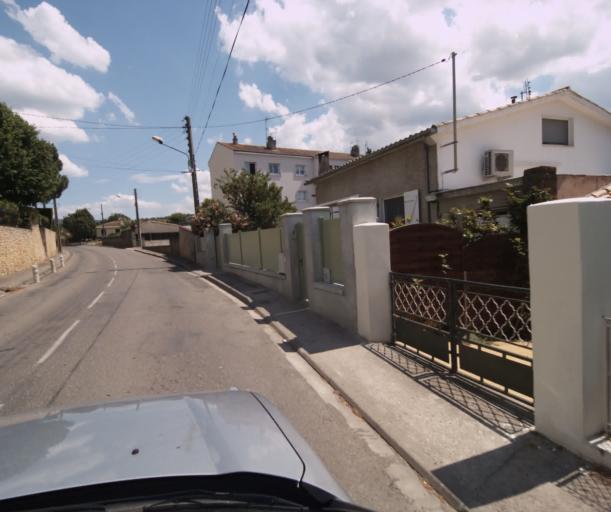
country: FR
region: Languedoc-Roussillon
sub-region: Departement de l'Aude
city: Limoux
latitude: 43.0491
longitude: 2.2235
